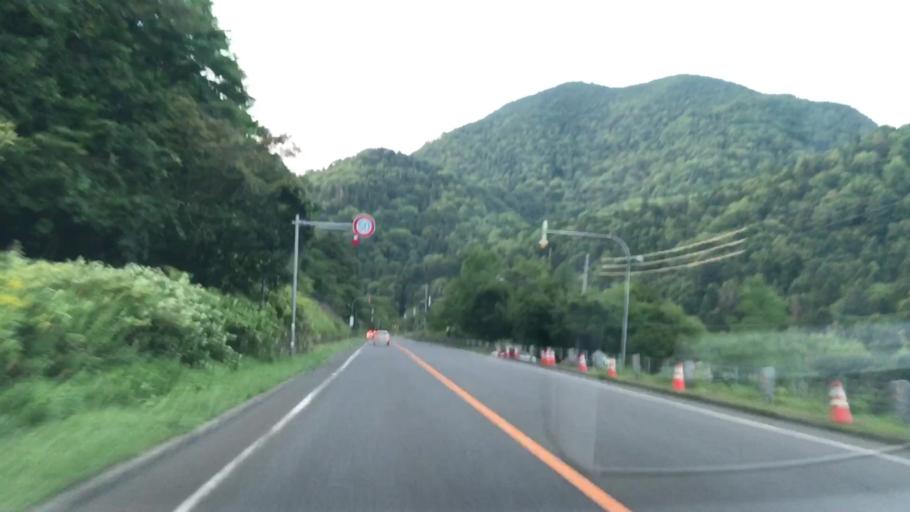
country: JP
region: Hokkaido
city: Sapporo
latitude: 42.9173
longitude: 141.1246
